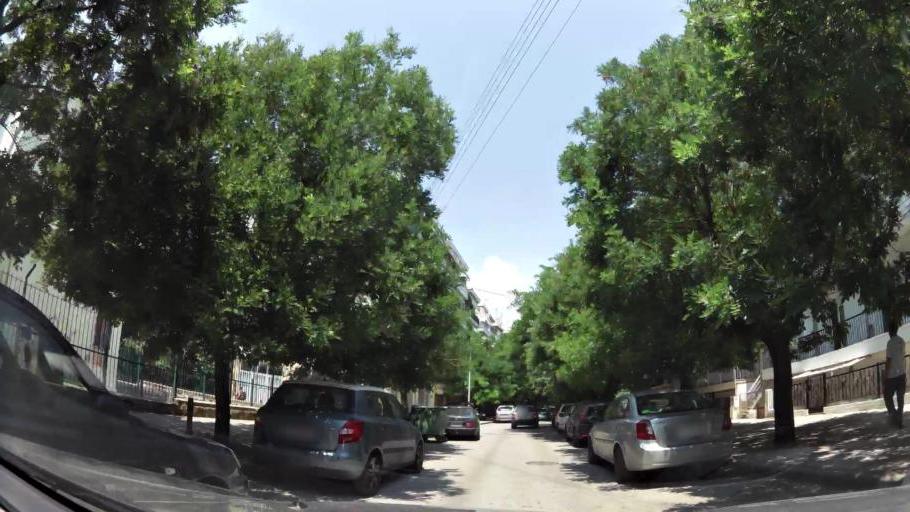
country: GR
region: Central Macedonia
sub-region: Nomos Thessalonikis
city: Thessaloniki
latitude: 40.6475
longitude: 22.9304
